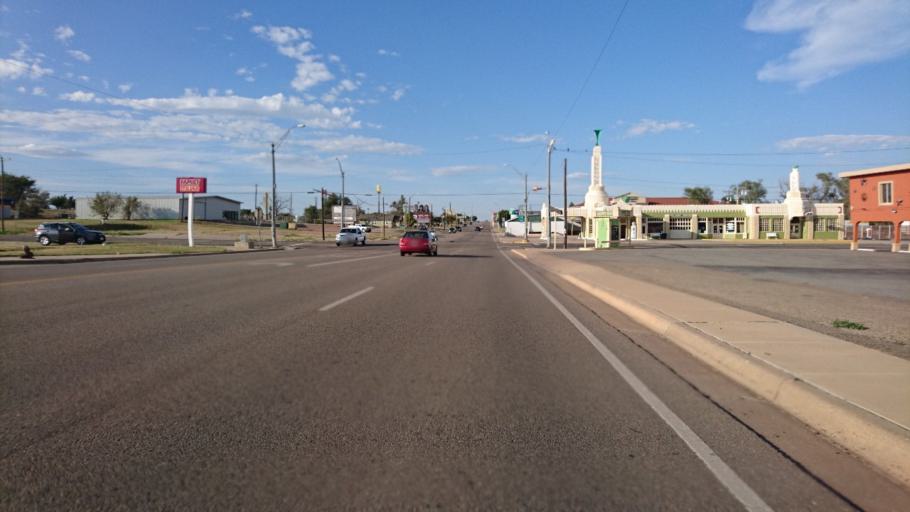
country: US
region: Texas
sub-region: Wheeler County
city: Shamrock
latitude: 35.2259
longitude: -100.2491
